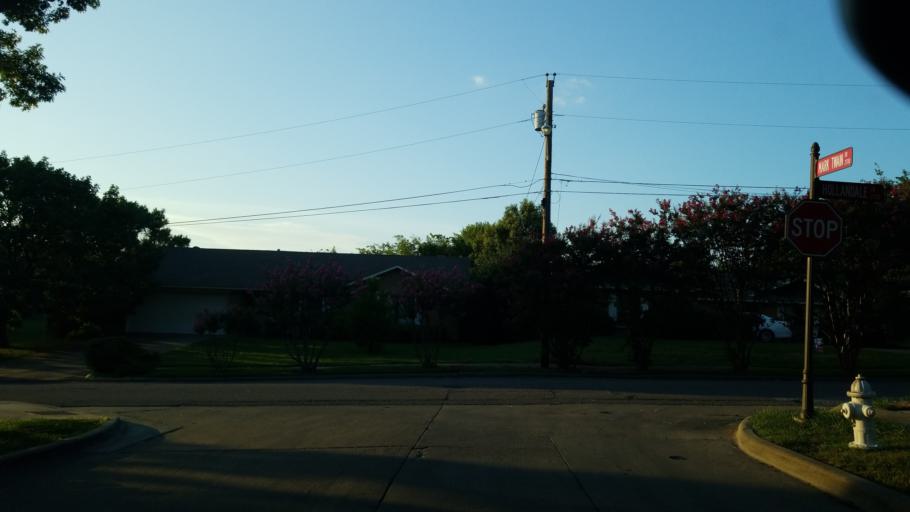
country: US
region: Texas
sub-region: Dallas County
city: Carrollton
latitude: 32.9430
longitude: -96.8844
